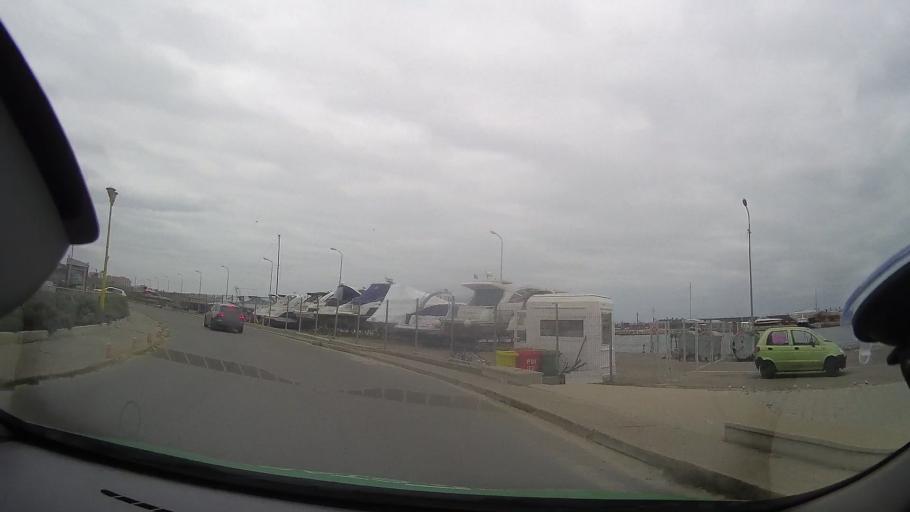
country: RO
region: Constanta
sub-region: Municipiul Constanta
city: Constanta
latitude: 44.1762
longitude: 28.6600
